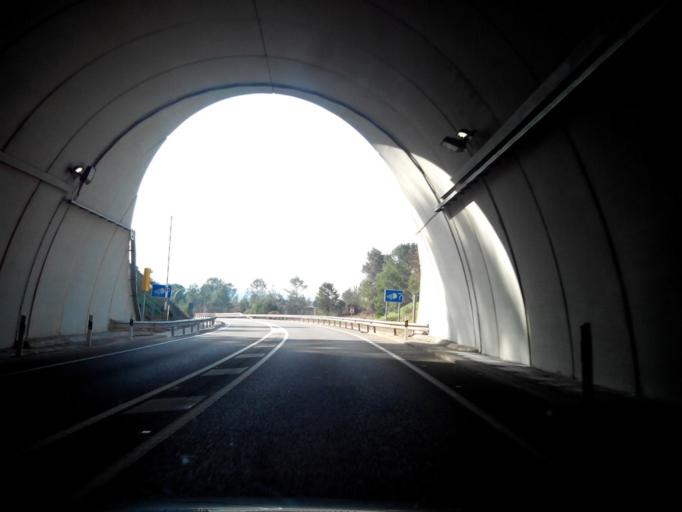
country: ES
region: Catalonia
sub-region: Provincia de Barcelona
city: Sant Salvador de Guardiola
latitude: 41.6816
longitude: 1.7539
